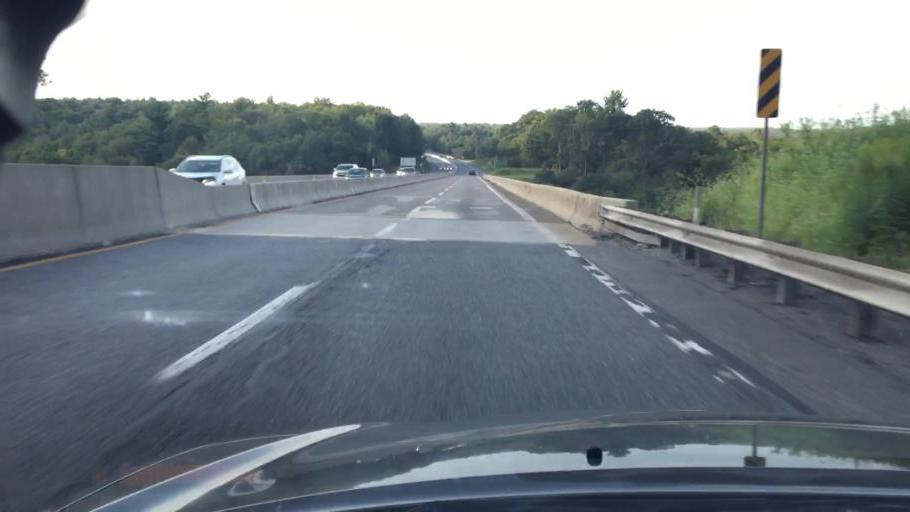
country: US
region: Pennsylvania
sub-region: Carbon County
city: Towamensing Trails
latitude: 41.0040
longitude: -75.6349
